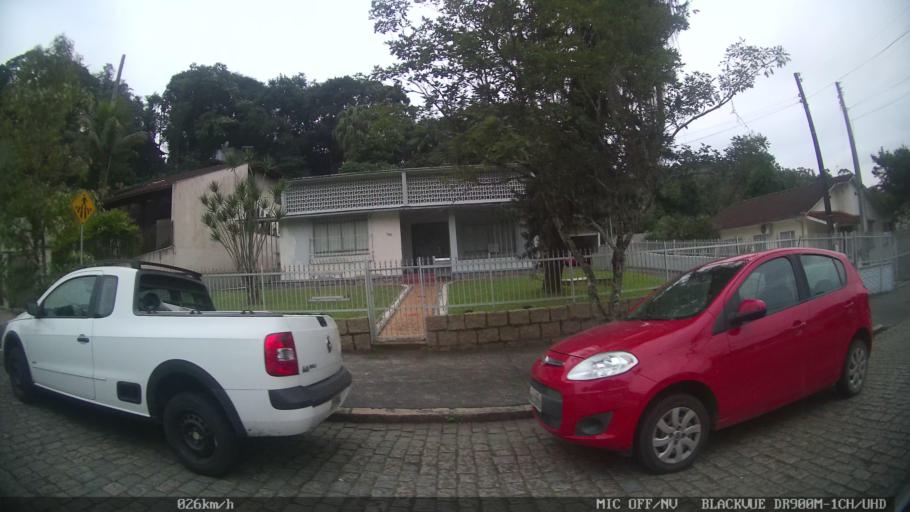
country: BR
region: Santa Catarina
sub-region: Joinville
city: Joinville
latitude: -26.2999
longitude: -48.8599
